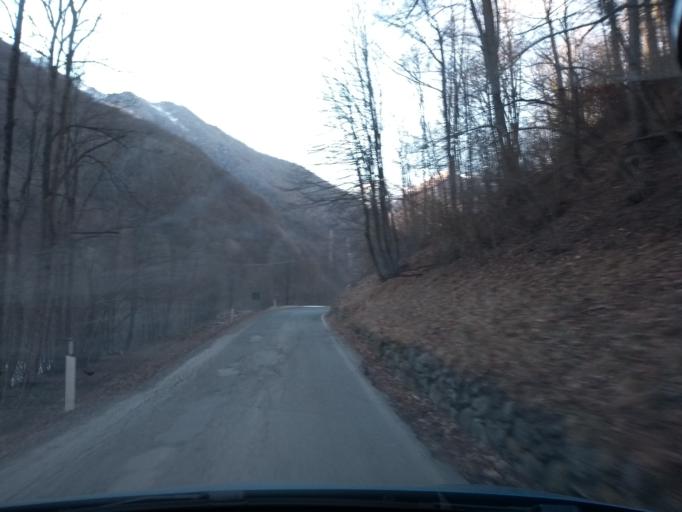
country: IT
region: Piedmont
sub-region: Provincia di Torino
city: Viu
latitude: 45.2293
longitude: 7.3454
